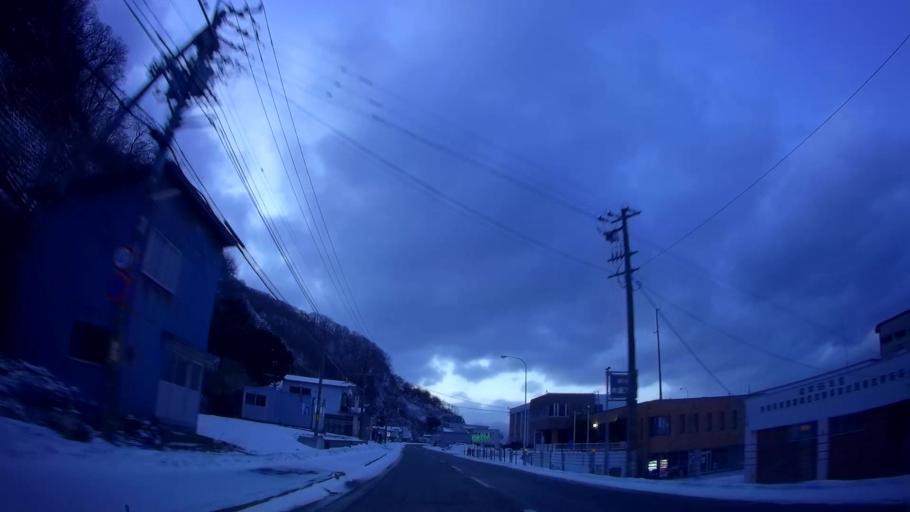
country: JP
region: Hokkaido
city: Hakodate
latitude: 41.8877
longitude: 141.0657
